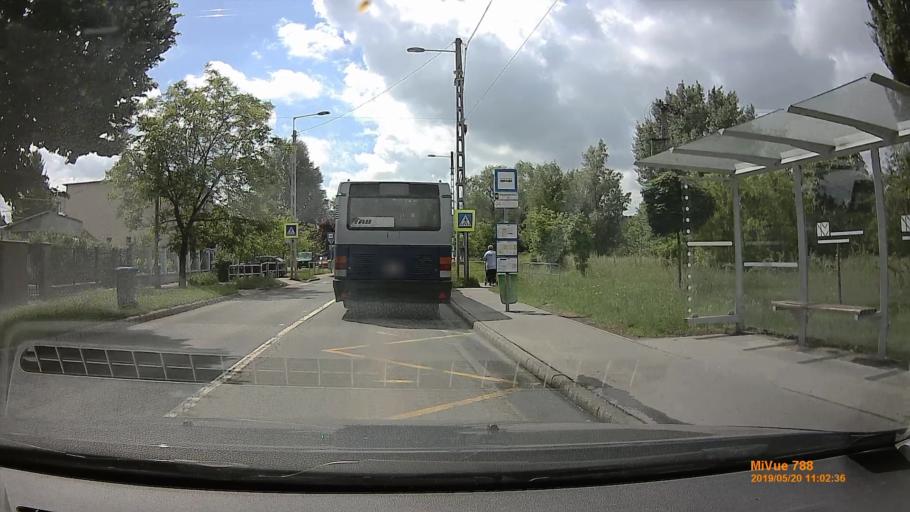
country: HU
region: Pest
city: Ecser
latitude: 47.4722
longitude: 19.2948
